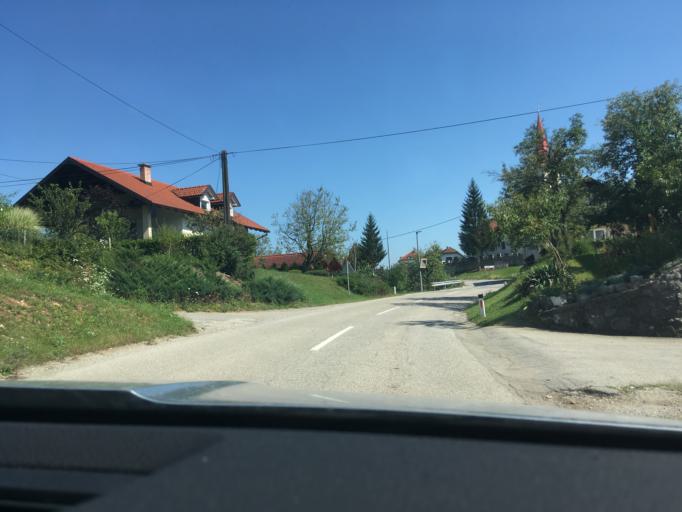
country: SI
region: Metlika
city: Metlika
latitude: 45.5232
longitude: 15.3099
